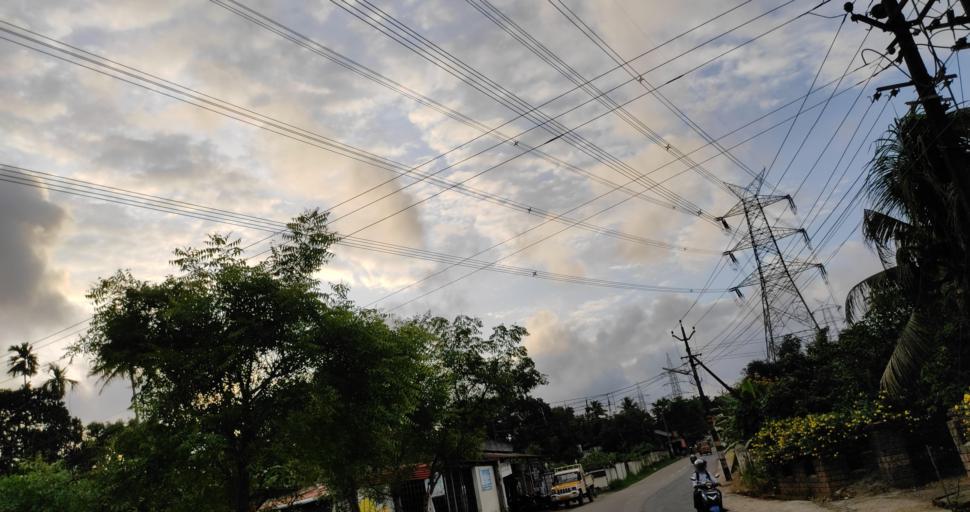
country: IN
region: Kerala
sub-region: Thrissur District
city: Kizhake Chalakudi
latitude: 10.3142
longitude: 76.3885
